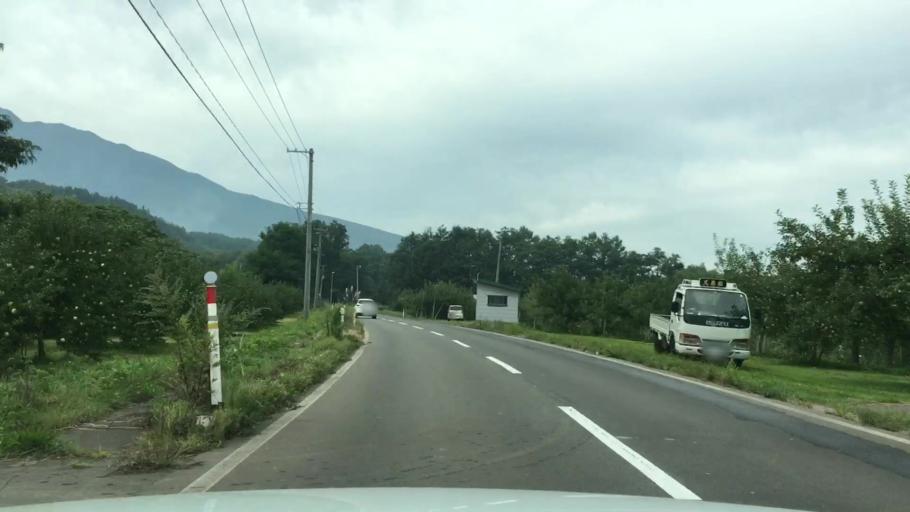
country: JP
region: Aomori
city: Hirosaki
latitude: 40.6685
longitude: 140.3923
